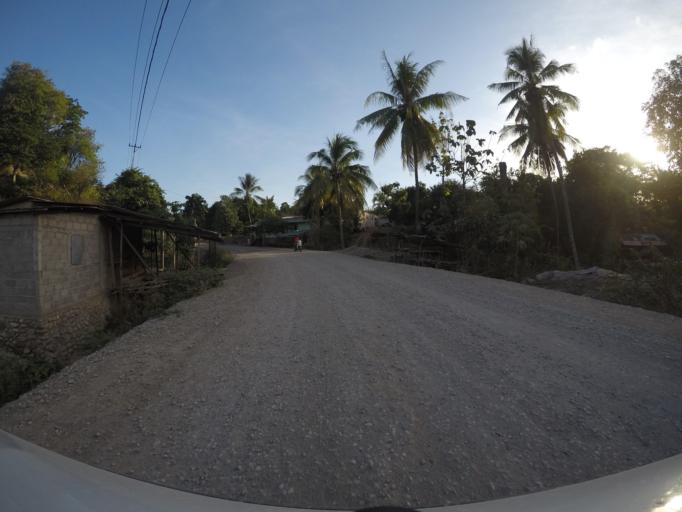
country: TL
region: Viqueque
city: Viqueque
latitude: -8.8336
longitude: 126.5192
